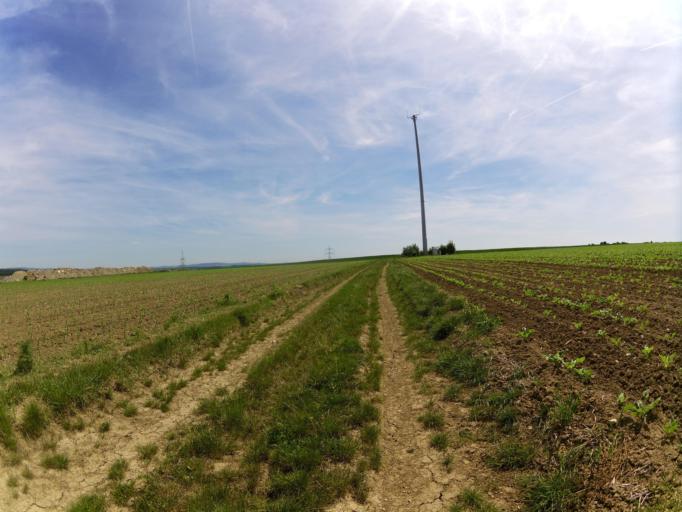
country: DE
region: Bavaria
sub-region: Regierungsbezirk Unterfranken
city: Sommerhausen
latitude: 49.6711
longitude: 10.0269
